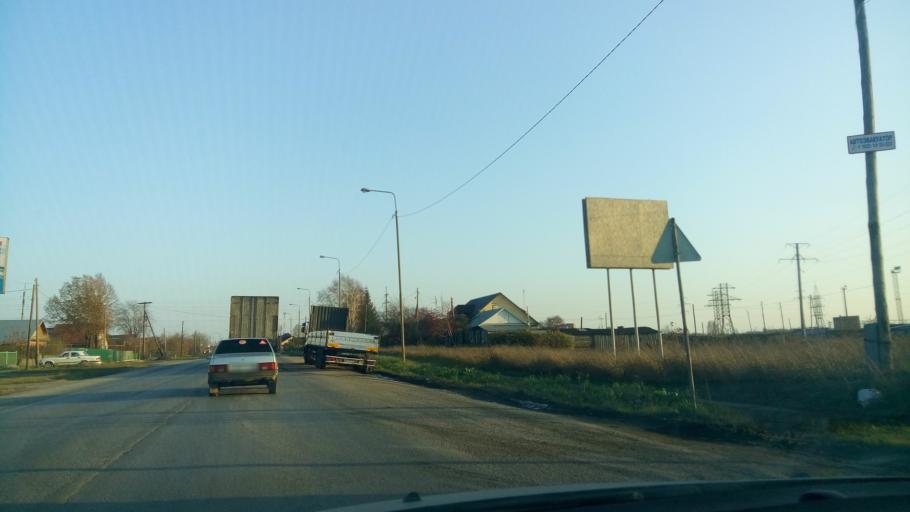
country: RU
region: Sverdlovsk
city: Bogdanovich
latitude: 56.7607
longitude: 62.0741
